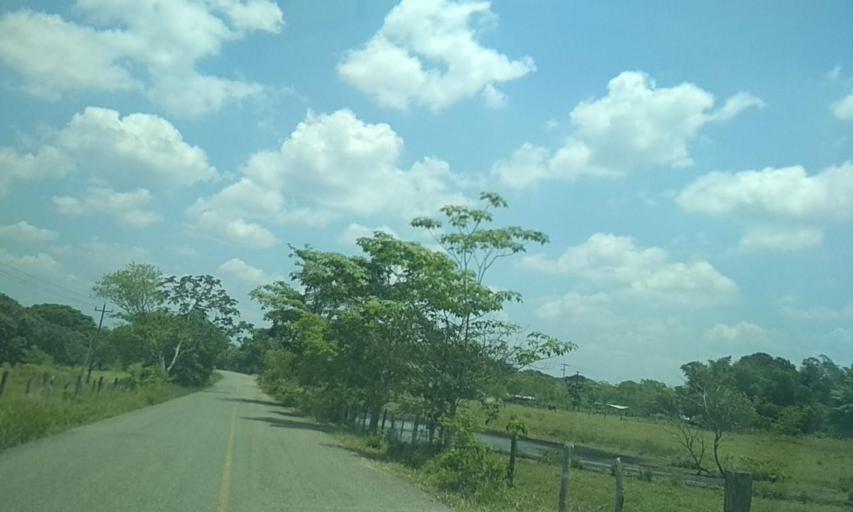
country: MX
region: Tabasco
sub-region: Huimanguillo
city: Francisco Rueda
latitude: 17.7931
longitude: -93.8514
